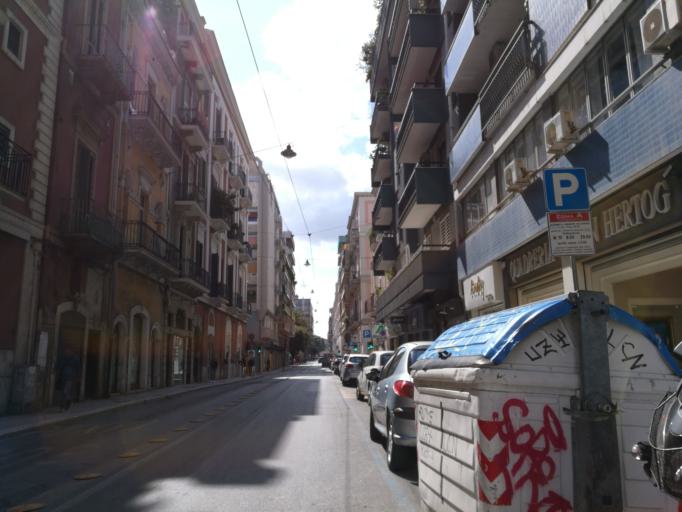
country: IT
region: Apulia
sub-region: Provincia di Bari
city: Bari
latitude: 41.1226
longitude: 16.8688
